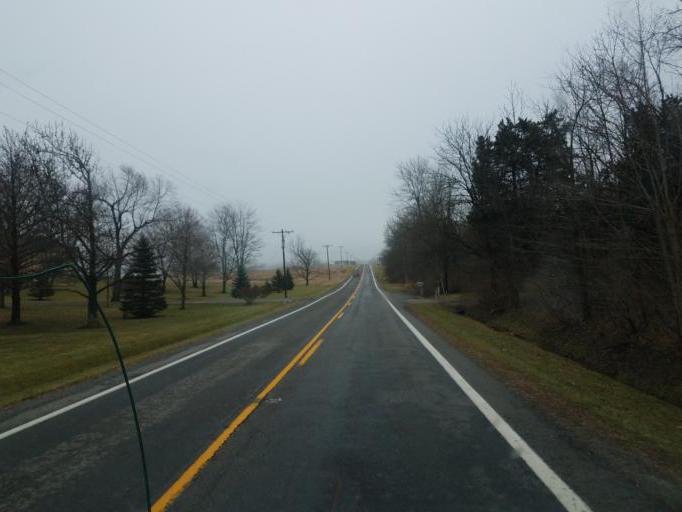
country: US
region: Ohio
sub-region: Champaign County
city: North Lewisburg
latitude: 40.2459
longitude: -83.5734
